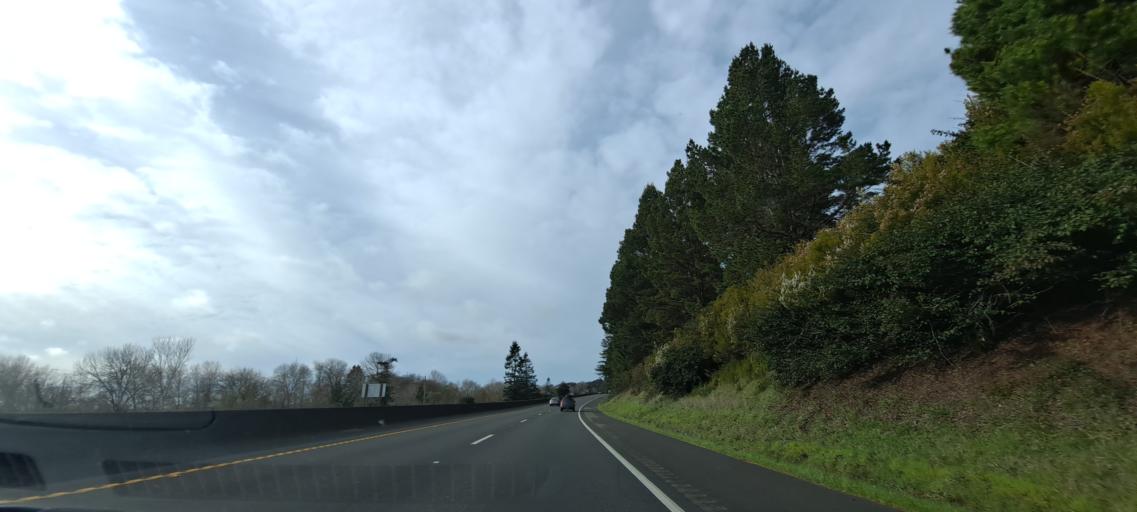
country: US
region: California
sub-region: Humboldt County
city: Fortuna
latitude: 40.6071
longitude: -124.1842
